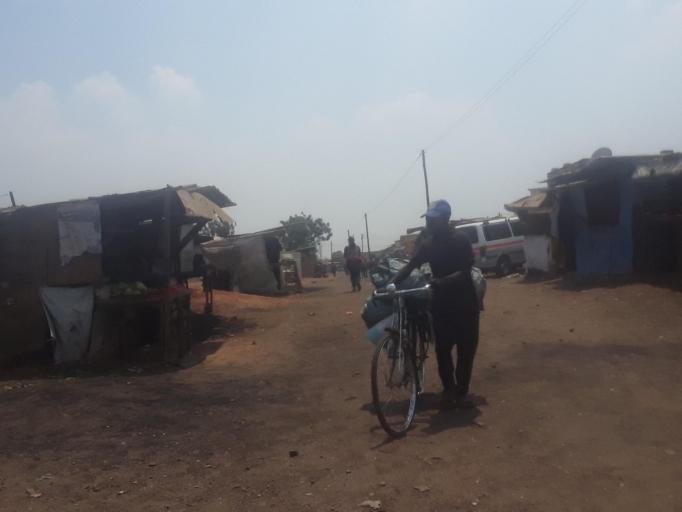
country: ZM
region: Lusaka
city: Lusaka
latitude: -15.3686
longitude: 28.2944
